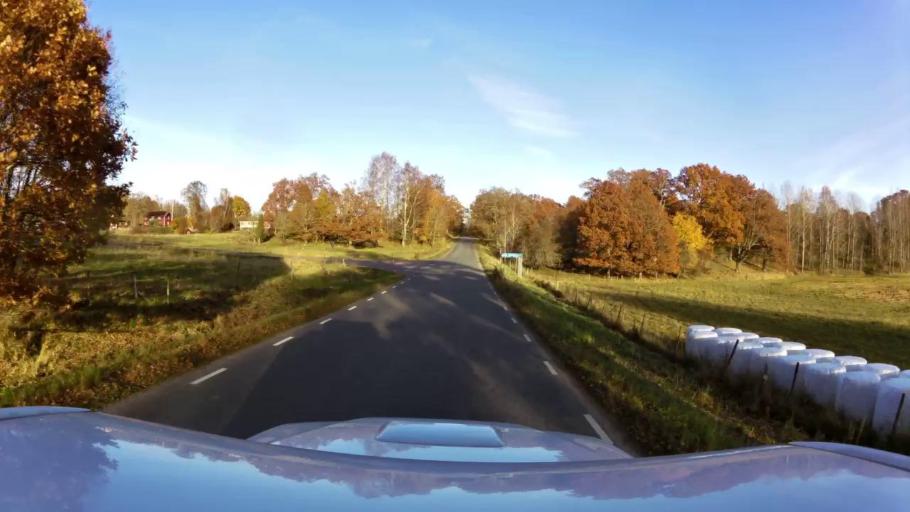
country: SE
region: OEstergoetland
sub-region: Linkopings Kommun
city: Sturefors
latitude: 58.3130
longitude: 15.6712
